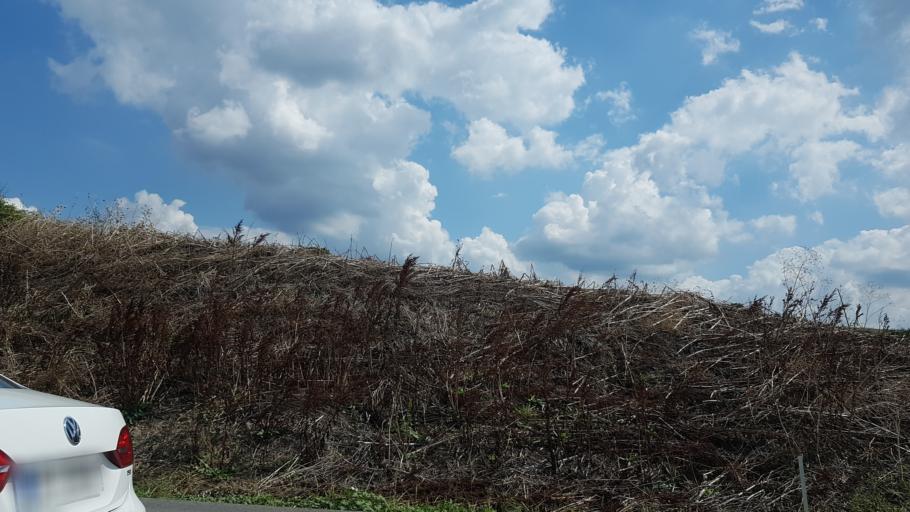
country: TR
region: Balikesir
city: Gobel
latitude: 40.0224
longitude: 28.2502
